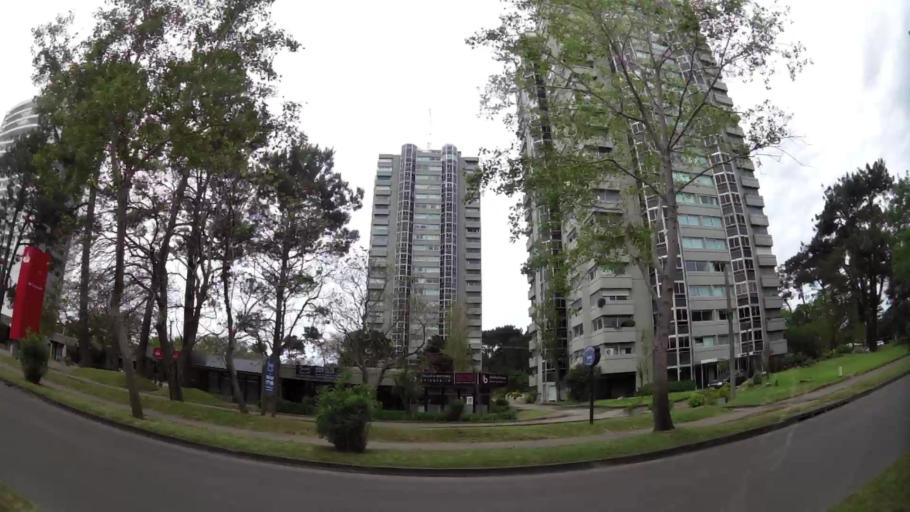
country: UY
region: Maldonado
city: Maldonado
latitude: -34.9326
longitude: -54.9415
